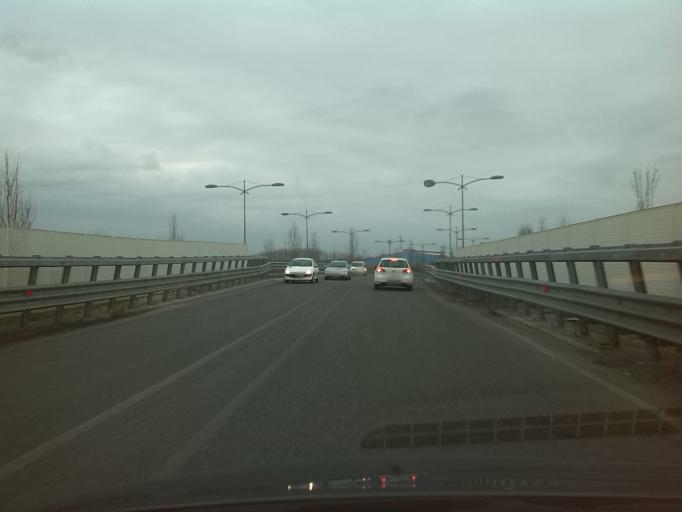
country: IT
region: Friuli Venezia Giulia
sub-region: Provincia di Gorizia
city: Villesse
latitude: 45.8688
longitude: 13.4362
